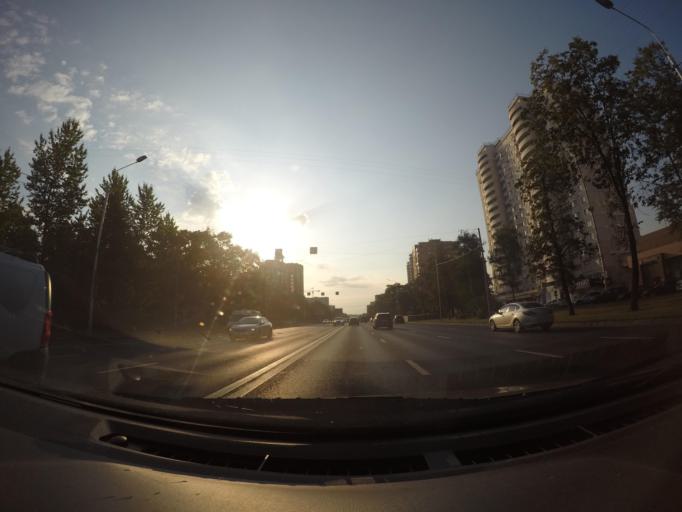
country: RU
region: Moscow
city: Novokuz'minki
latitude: 55.7043
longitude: 37.7737
